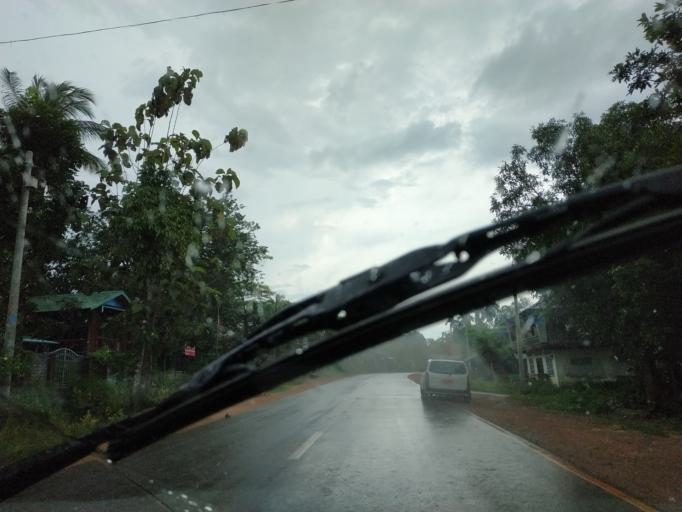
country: MM
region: Tanintharyi
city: Dawei
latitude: 13.8898
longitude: 98.2579
